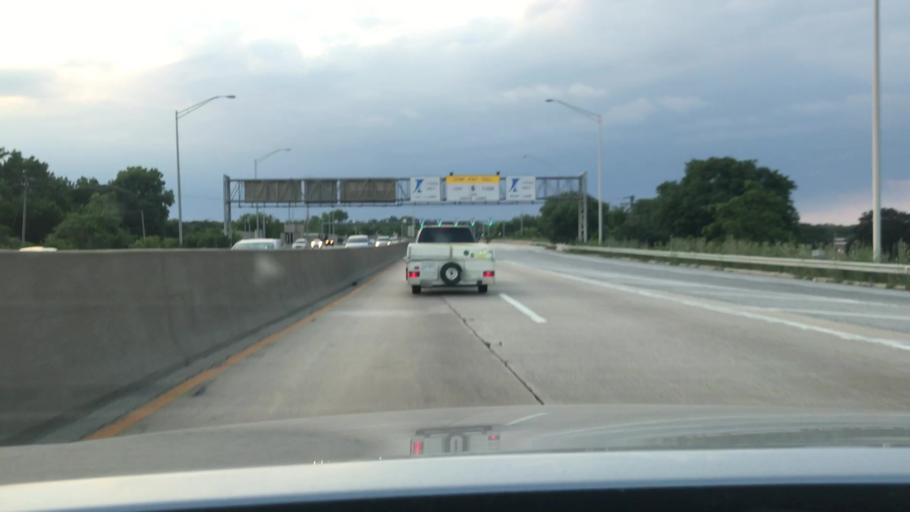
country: US
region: Illinois
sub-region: Cook County
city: Indian Head Park
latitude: 41.7633
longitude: -87.9050
